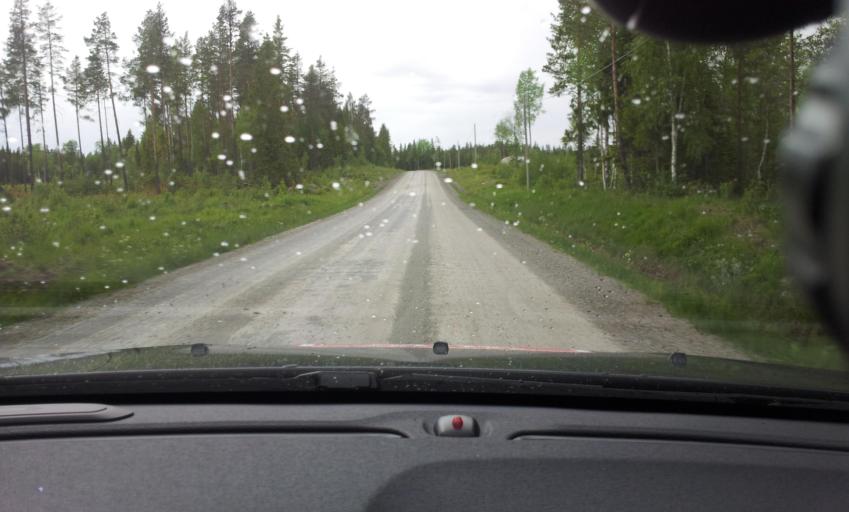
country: SE
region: Jaemtland
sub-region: OEstersunds Kommun
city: Brunflo
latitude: 63.1077
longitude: 15.0349
